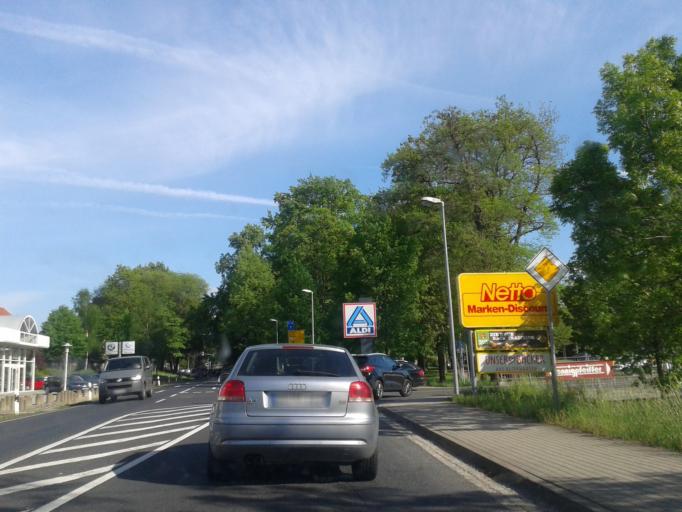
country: DE
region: Saxony
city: Wilsdruff
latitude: 51.0571
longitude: 13.5327
